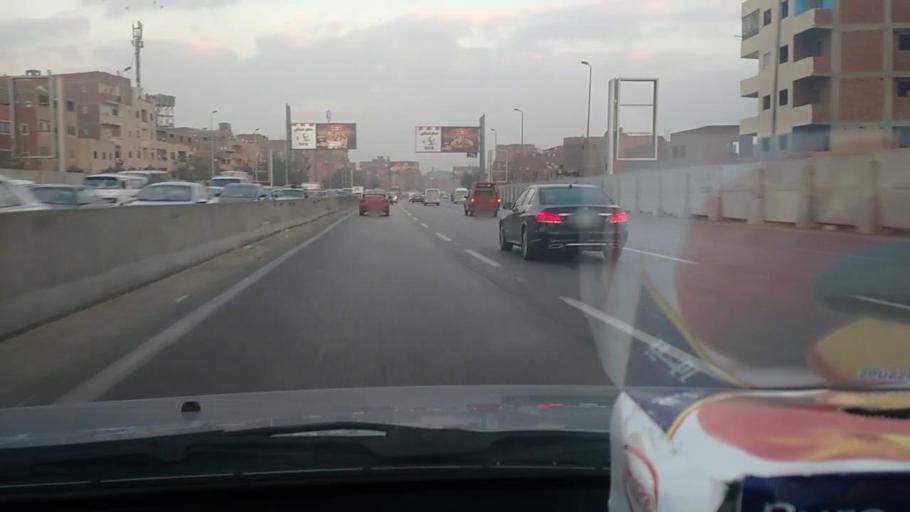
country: EG
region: Al Jizah
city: Al Jizah
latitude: 29.9927
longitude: 31.2456
